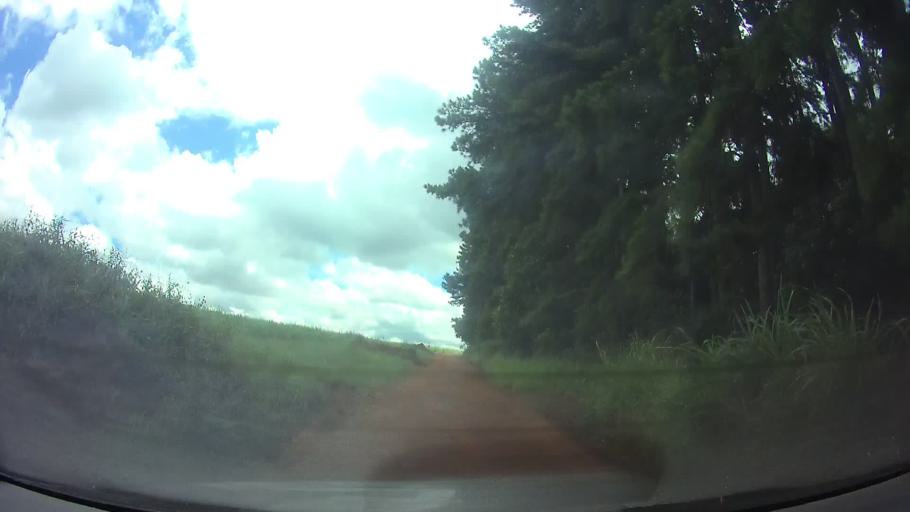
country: PY
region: Paraguari
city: La Colmena
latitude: -25.9525
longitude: -56.7738
